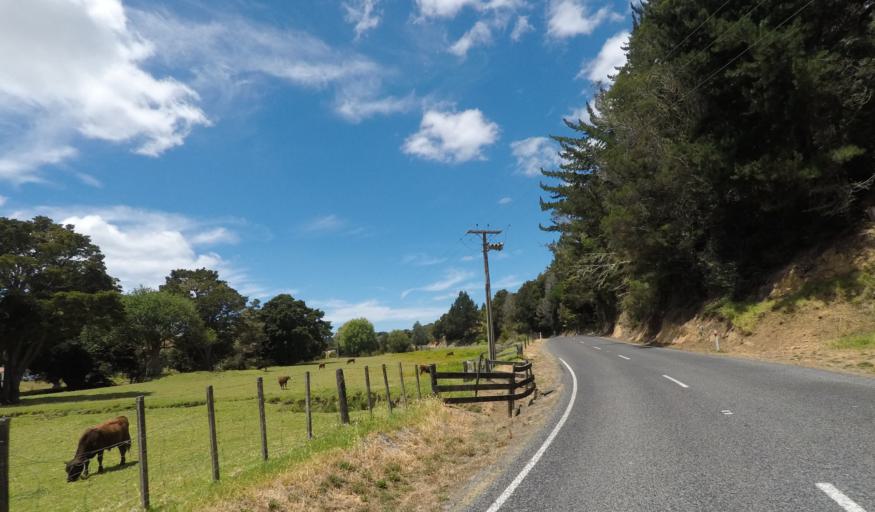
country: NZ
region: Northland
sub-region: Whangarei
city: Ngunguru
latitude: -35.5054
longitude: 174.4104
